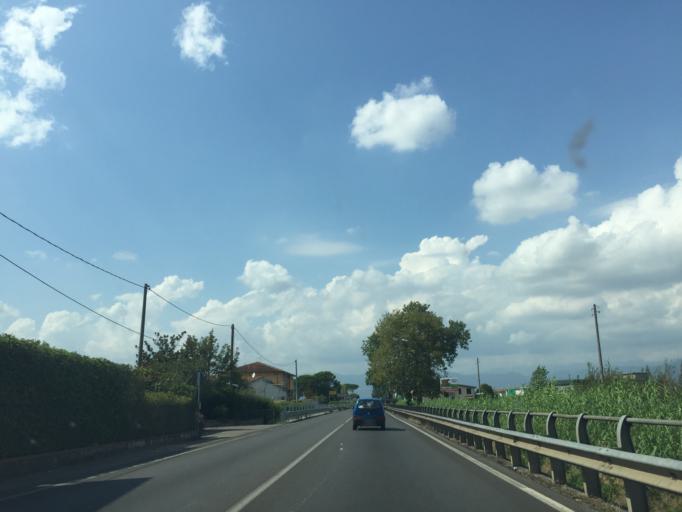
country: IT
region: Tuscany
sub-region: Provincia di Pistoia
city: Vignole-Olmi
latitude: 43.8713
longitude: 10.9854
